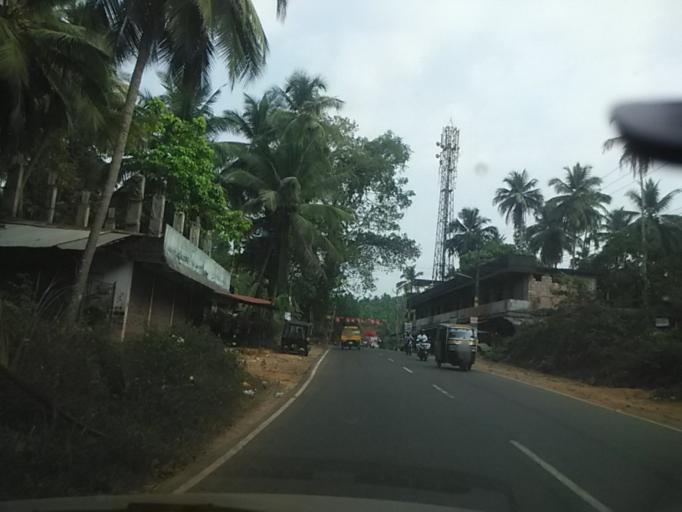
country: IN
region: Kerala
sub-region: Kozhikode
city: Naduvannur
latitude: 11.5452
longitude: 75.7676
